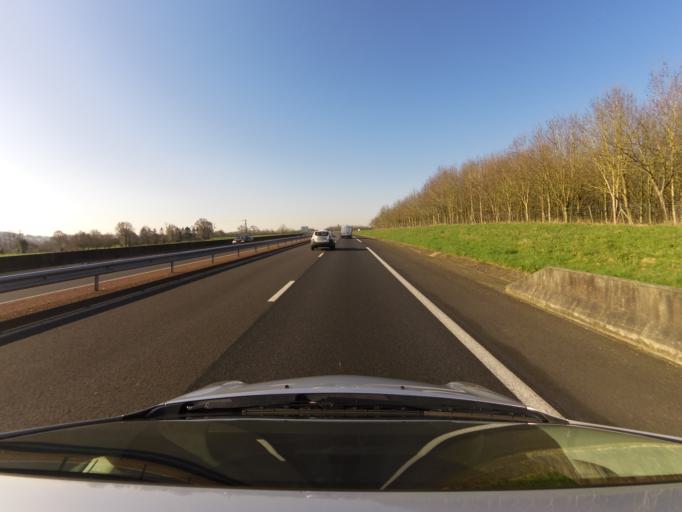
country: FR
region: Lower Normandy
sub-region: Departement de la Manche
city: Saint-James
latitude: 48.5694
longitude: -1.3342
